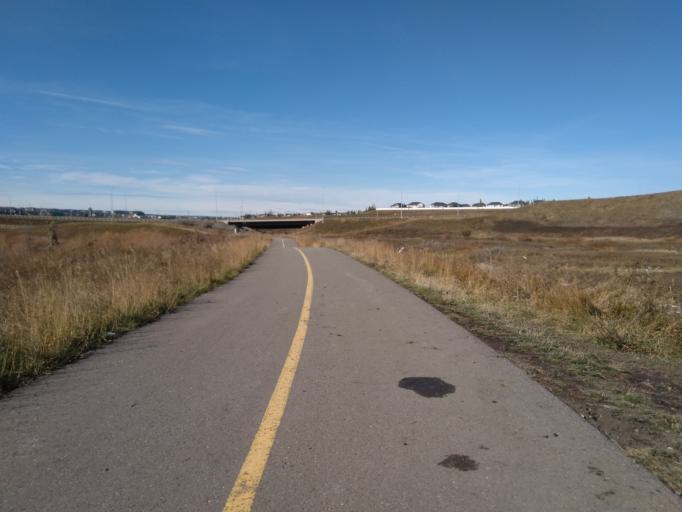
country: CA
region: Alberta
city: Calgary
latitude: 51.1569
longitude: -114.1091
